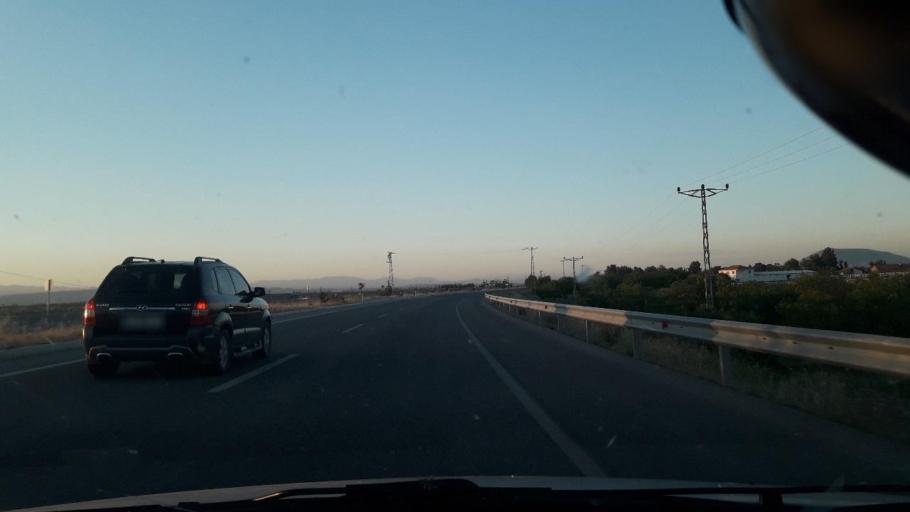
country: TR
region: Malatya
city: Yazihan
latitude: 38.4917
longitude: 38.2166
